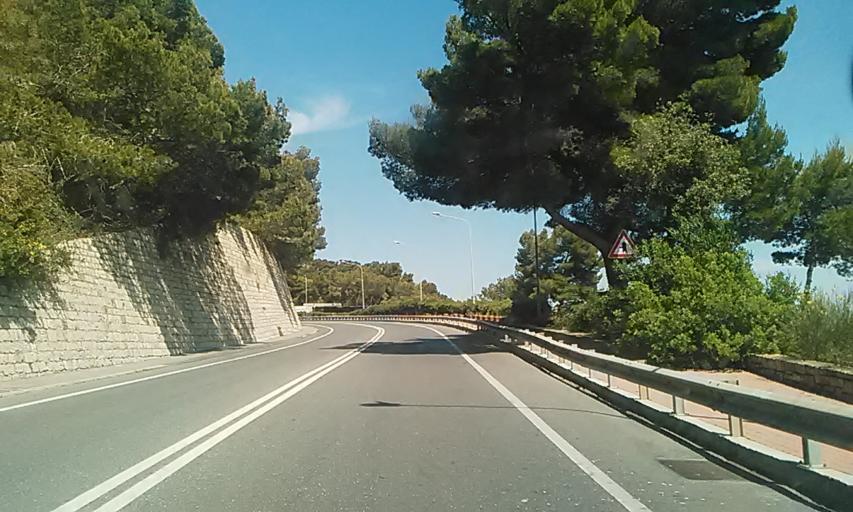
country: IT
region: Liguria
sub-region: Provincia di Savona
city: Marina di Andora
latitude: 43.9528
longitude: 8.1579
